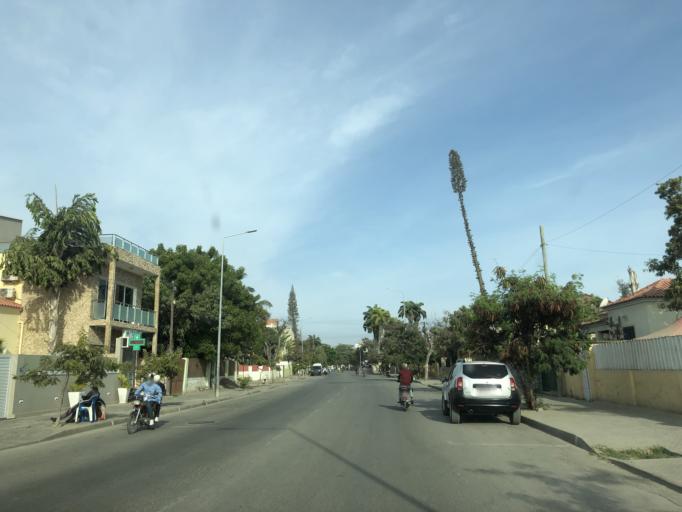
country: AO
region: Benguela
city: Benguela
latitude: -12.5737
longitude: 13.4038
